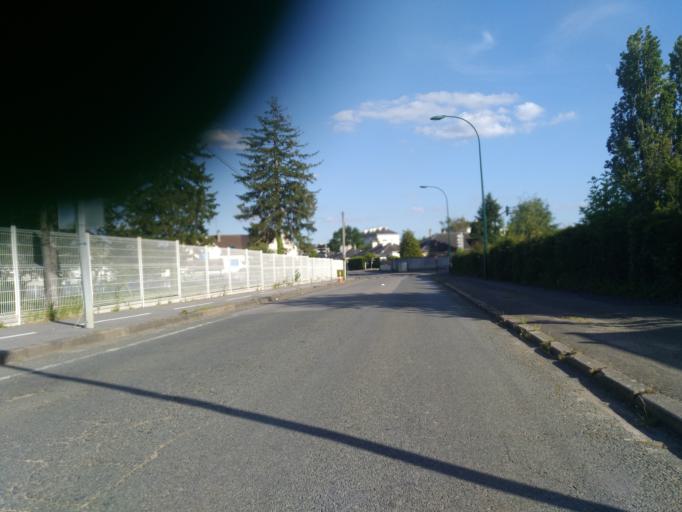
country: FR
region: Ile-de-France
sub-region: Departement des Yvelines
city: Plaisir
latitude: 48.8241
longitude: 1.9401
